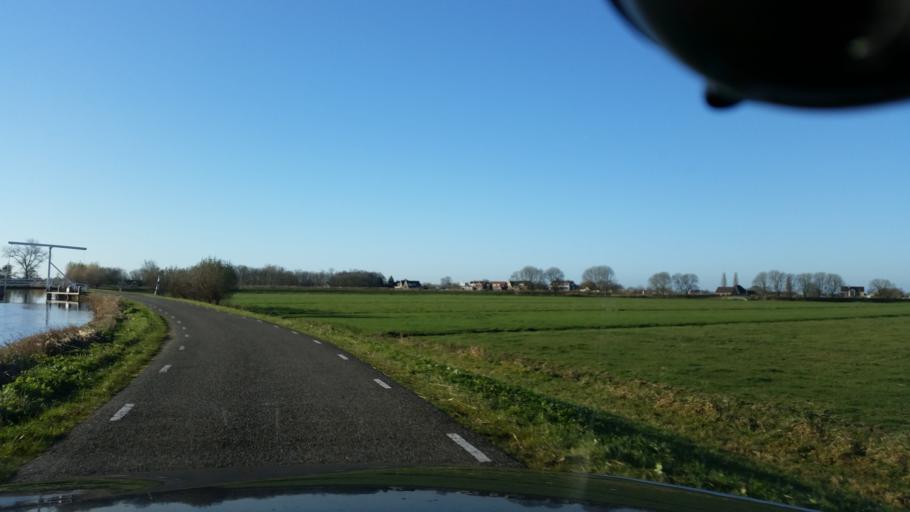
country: NL
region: Utrecht
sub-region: Gemeente De Ronde Venen
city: Mijdrecht
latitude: 52.2529
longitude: 4.8778
